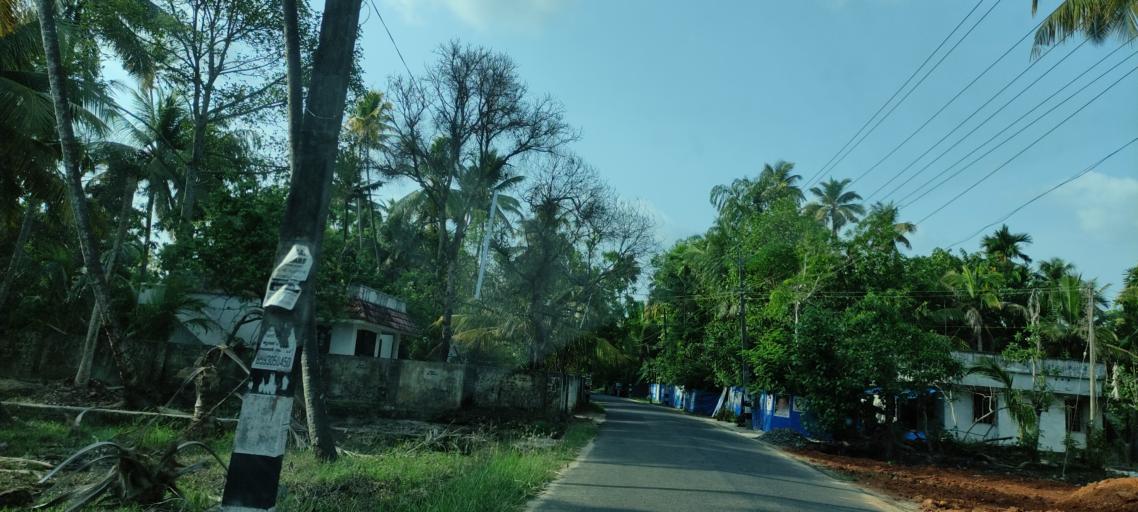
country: IN
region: Kerala
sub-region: Alappuzha
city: Vayalar
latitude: 9.7237
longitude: 76.2871
